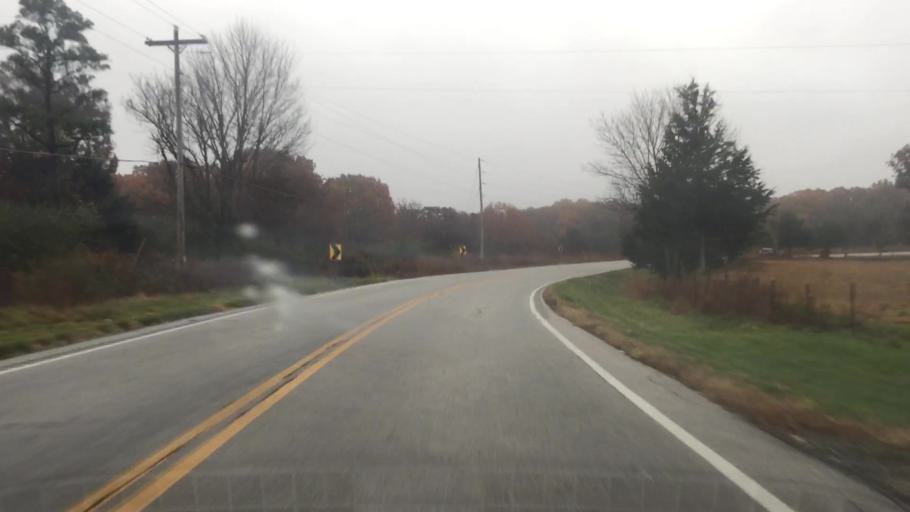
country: US
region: Missouri
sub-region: Callaway County
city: Fulton
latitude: 38.8769
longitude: -92.0758
